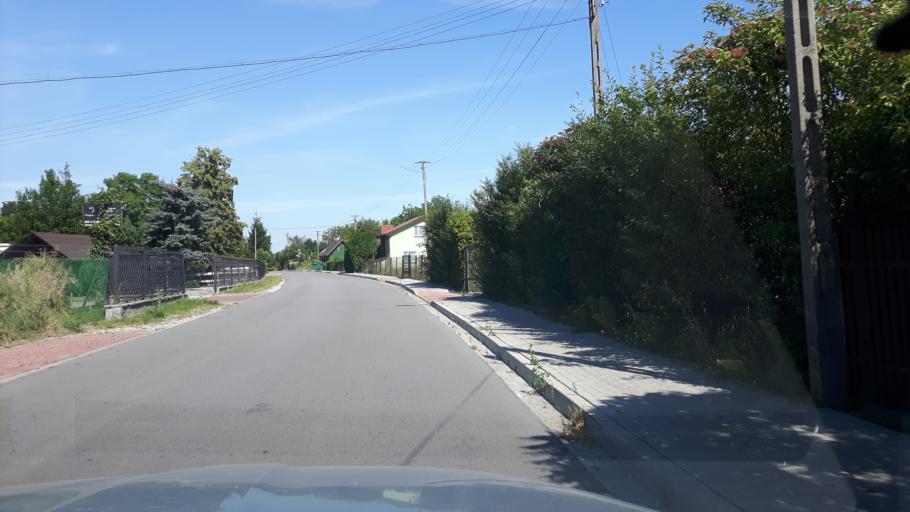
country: PL
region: Masovian Voivodeship
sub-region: Powiat nowodworski
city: Zakroczym
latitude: 52.4910
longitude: 20.6269
